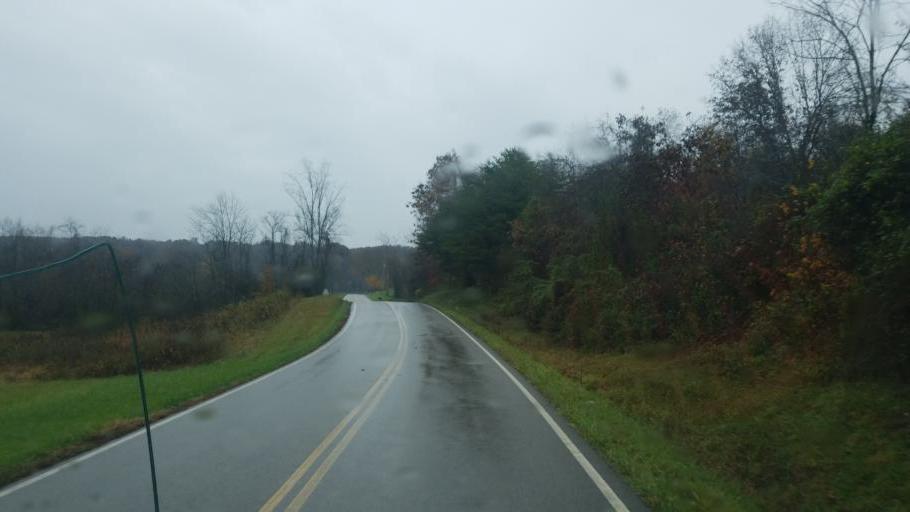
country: US
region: West Virginia
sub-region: Wood County
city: Blennerhassett
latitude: 39.3303
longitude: -81.6211
